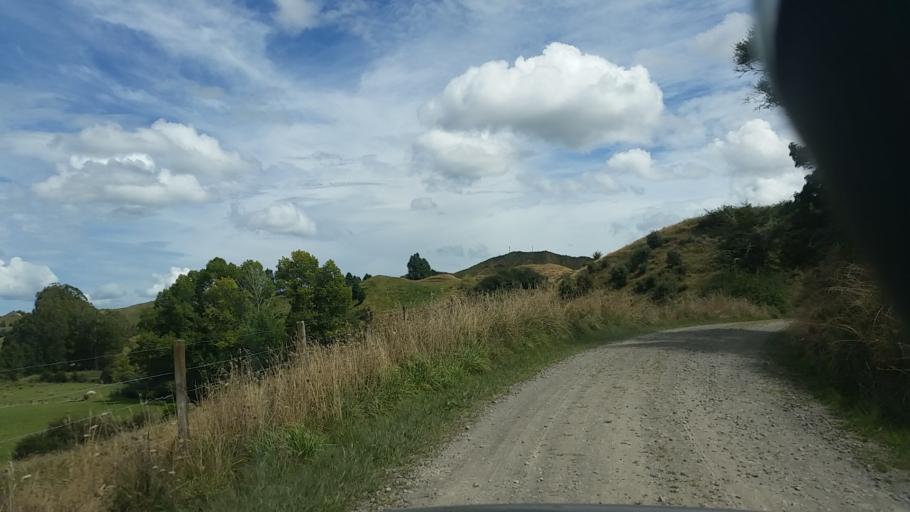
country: NZ
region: Taranaki
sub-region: South Taranaki District
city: Eltham
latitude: -39.2561
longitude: 174.5687
